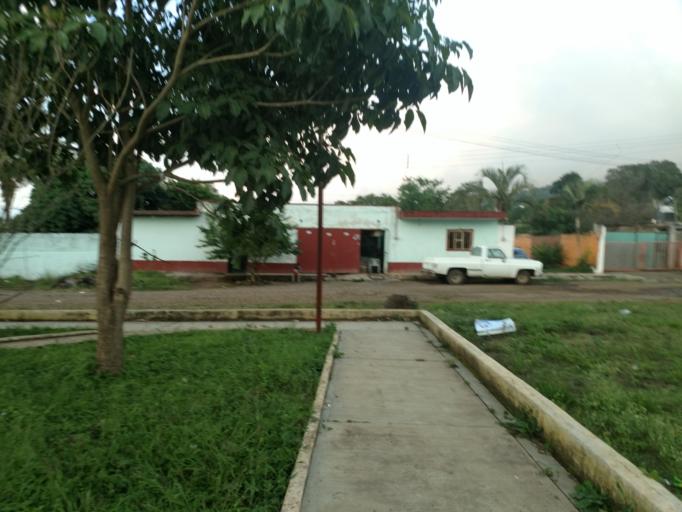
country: MX
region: Nayarit
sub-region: Tepic
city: La Corregidora
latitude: 21.4614
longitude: -104.8024
